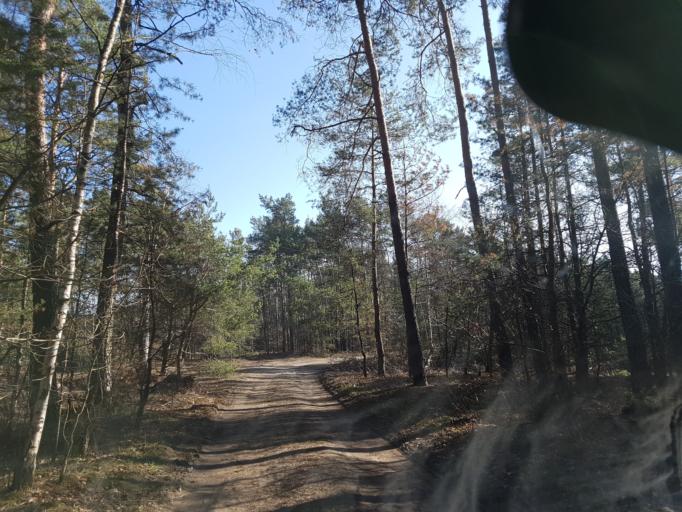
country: DE
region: Brandenburg
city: Trobitz
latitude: 51.5429
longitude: 13.4557
